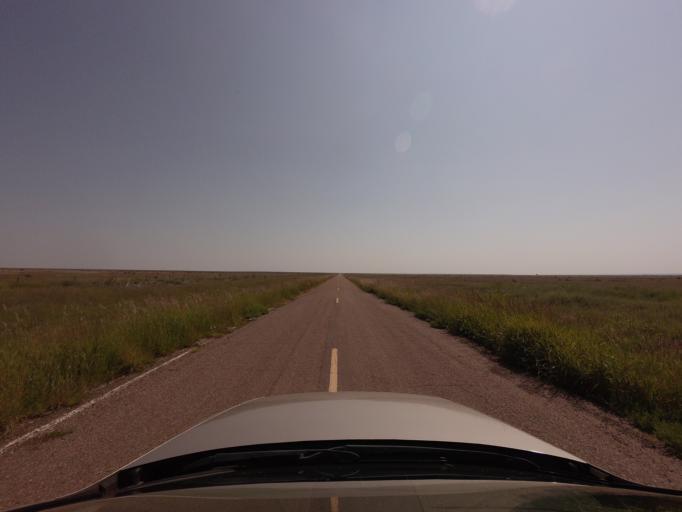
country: US
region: New Mexico
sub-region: Curry County
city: Cannon Air Force Base
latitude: 34.6333
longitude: -103.4245
